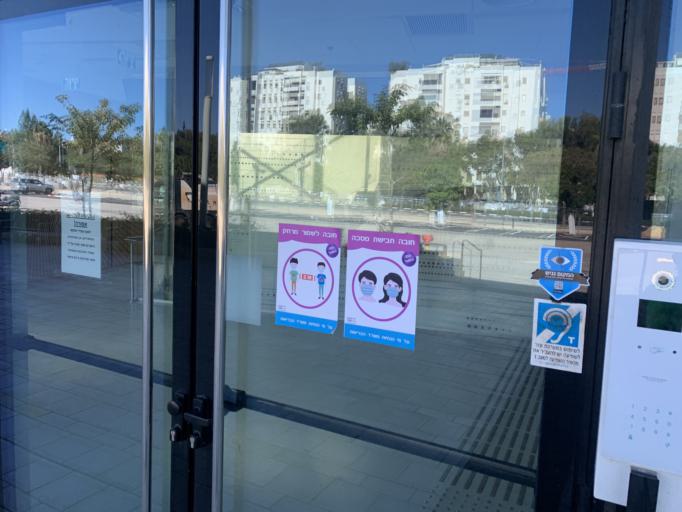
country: IL
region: Tel Aviv
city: Ramat Gan
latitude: 32.1058
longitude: 34.8237
